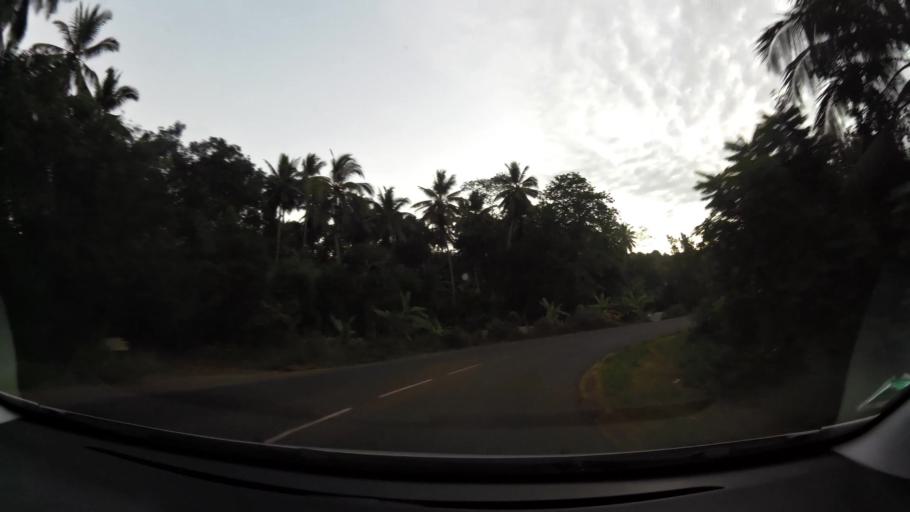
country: YT
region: Bandraboua
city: Bandraboua
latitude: -12.7310
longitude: 45.1310
